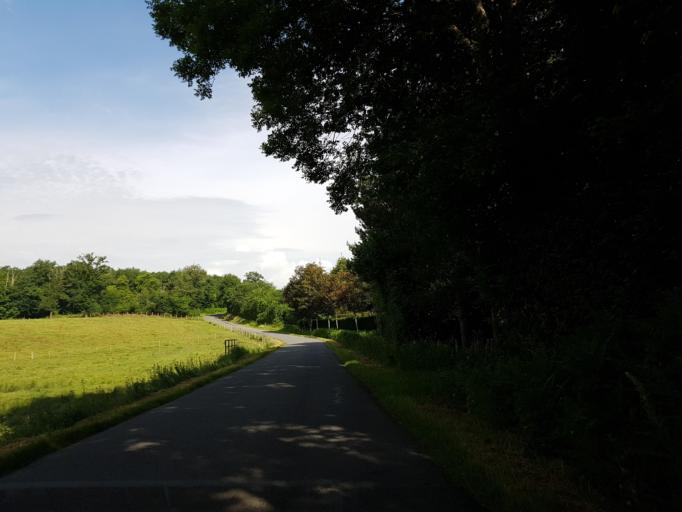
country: FR
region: Poitou-Charentes
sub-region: Departement de la Charente
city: Exideuil
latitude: 45.8969
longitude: 0.6878
